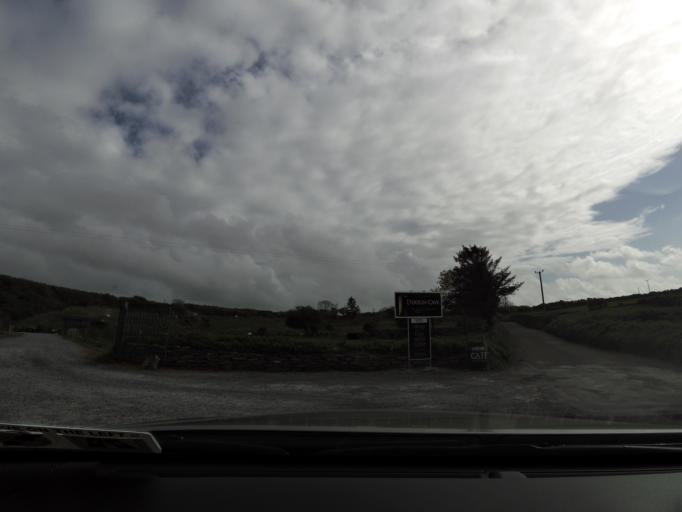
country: IE
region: Connaught
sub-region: County Galway
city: Bearna
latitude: 53.0422
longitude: -9.3459
